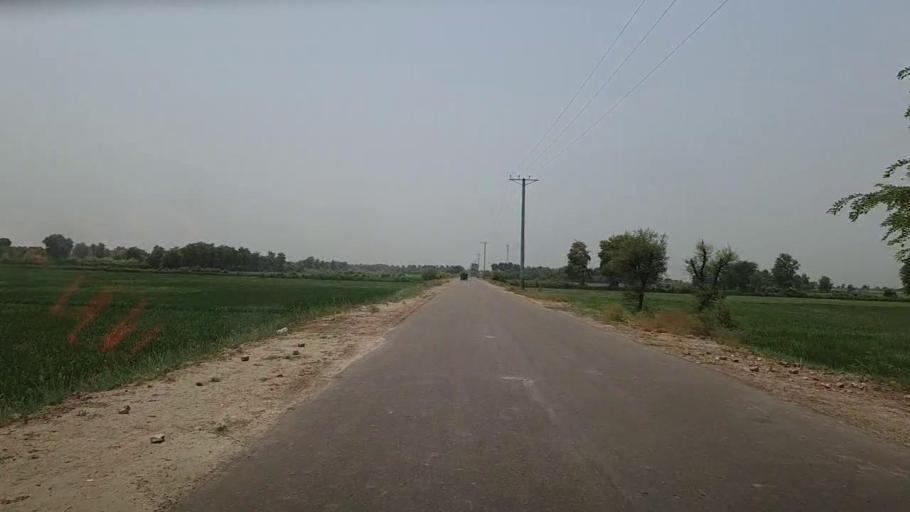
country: PK
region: Sindh
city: Sita Road
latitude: 27.0485
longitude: 67.9014
